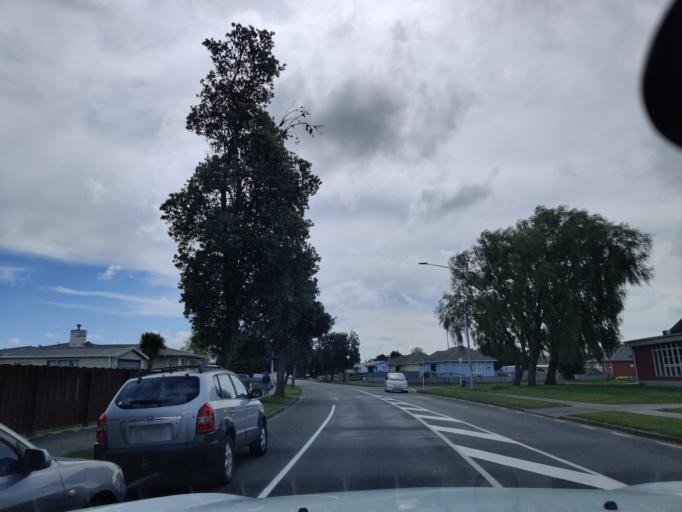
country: NZ
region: Manawatu-Wanganui
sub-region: Palmerston North City
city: Palmerston North
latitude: -40.3591
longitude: 175.5862
